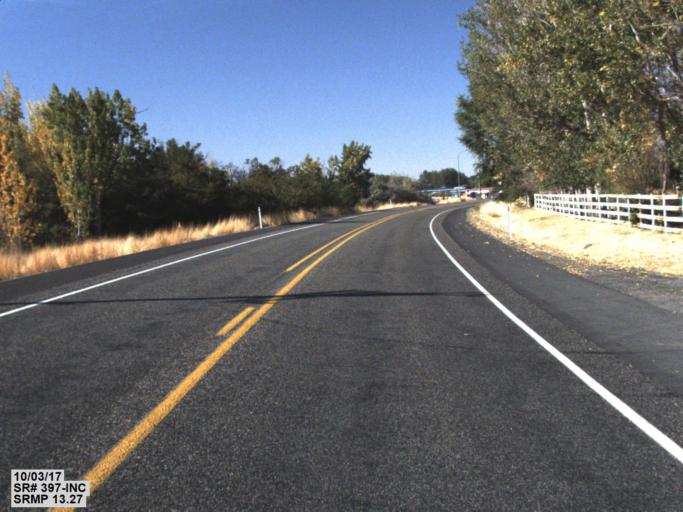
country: US
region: Washington
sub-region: Benton County
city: Finley
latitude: 46.1663
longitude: -119.0474
